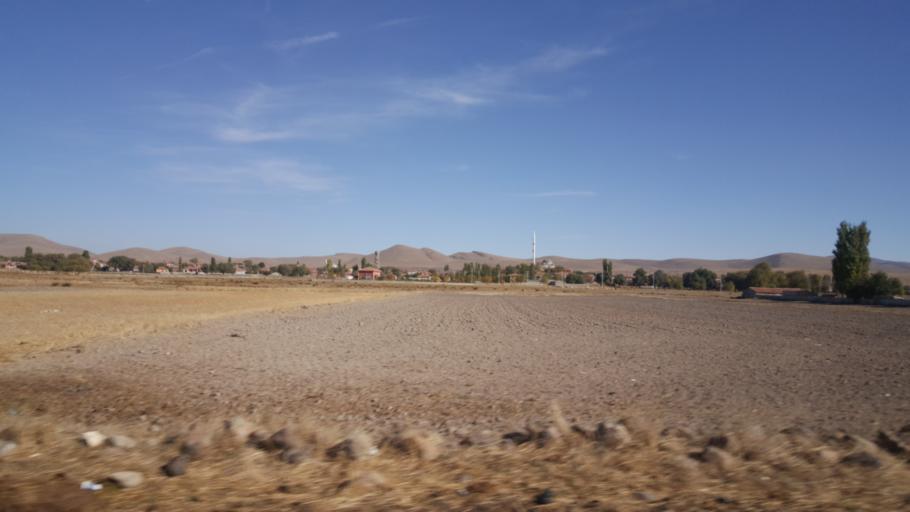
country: TR
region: Ankara
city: Altpinar
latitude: 39.2640
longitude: 32.7530
